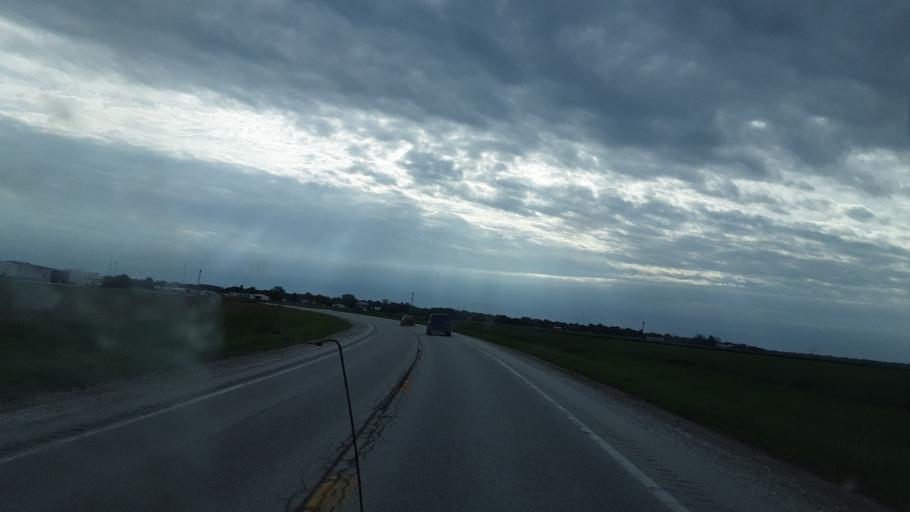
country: US
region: Illinois
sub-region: Hancock County
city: Carthage
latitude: 40.4093
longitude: -91.1629
